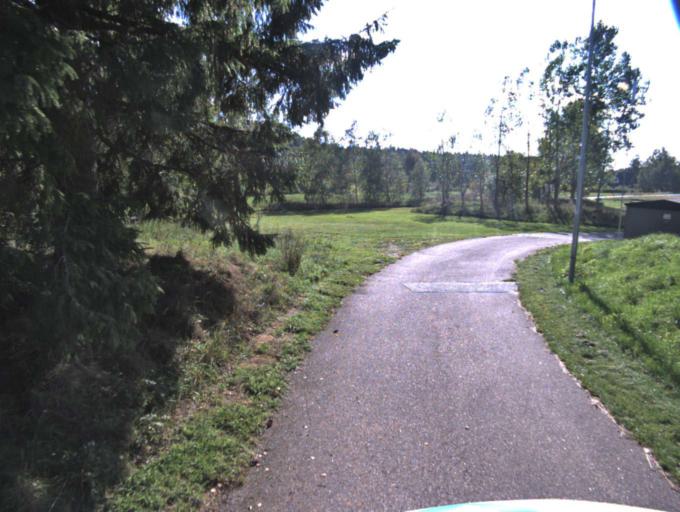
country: SE
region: Vaestra Goetaland
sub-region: Boras Kommun
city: Dalsjofors
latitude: 57.8275
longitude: 13.1849
